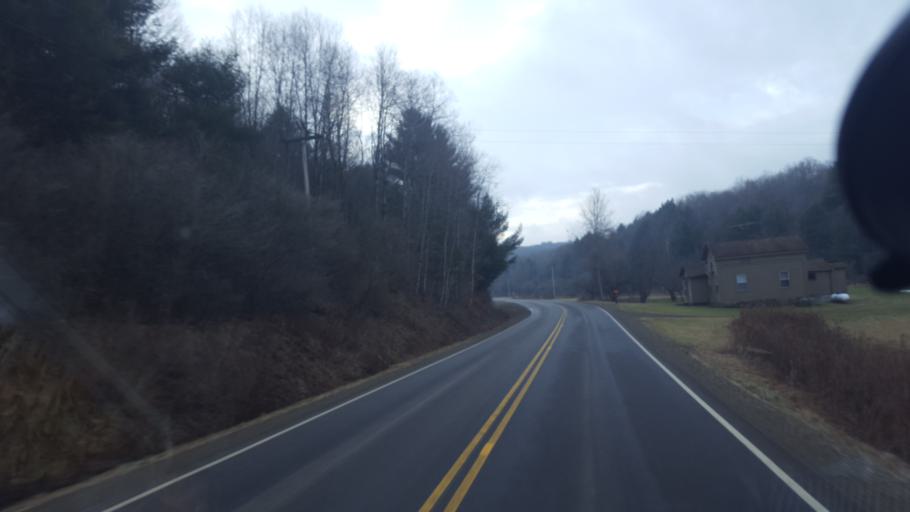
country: US
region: New York
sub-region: Allegany County
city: Andover
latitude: 42.0342
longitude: -77.7543
